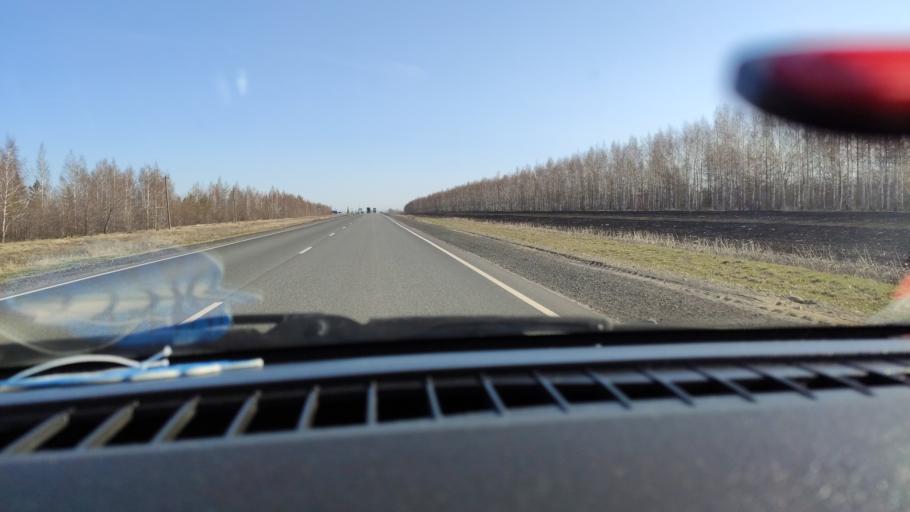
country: RU
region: Samara
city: Syzran'
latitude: 52.9893
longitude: 48.3204
